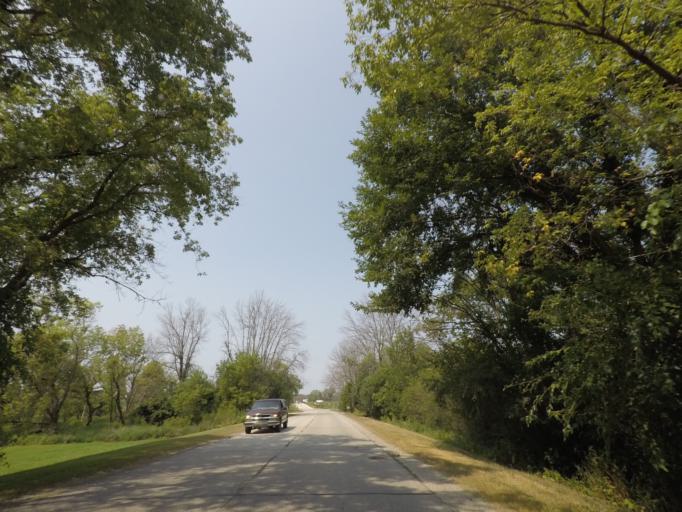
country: US
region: Wisconsin
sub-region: Waukesha County
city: Oconomowoc
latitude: 43.0688
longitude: -88.5529
